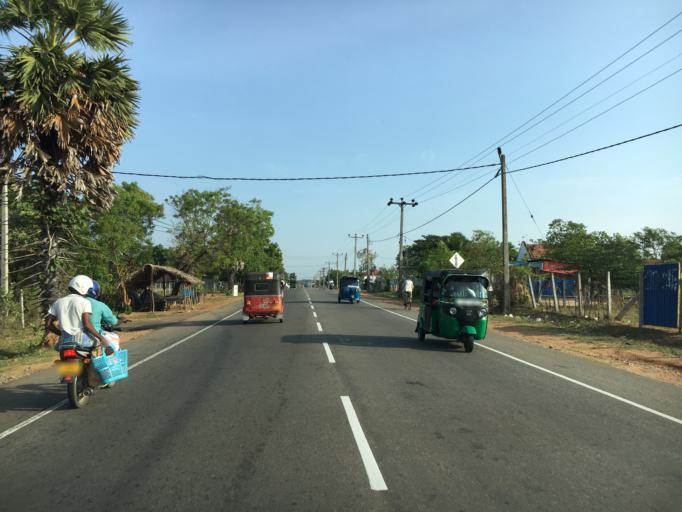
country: LK
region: Eastern Province
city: Eravur Town
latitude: 7.9289
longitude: 81.5129
